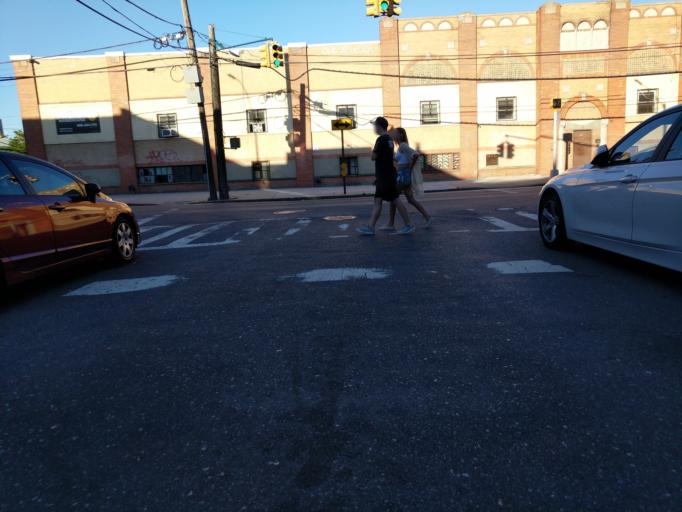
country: US
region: New York
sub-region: Queens County
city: Long Island City
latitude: 40.7193
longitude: -73.9409
